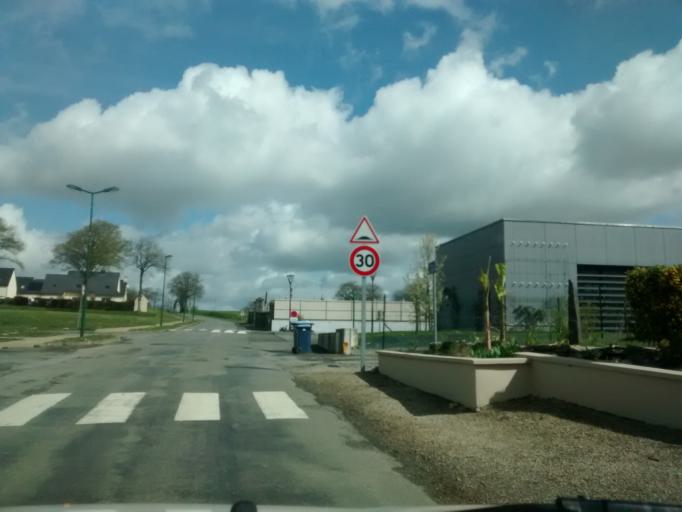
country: FR
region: Brittany
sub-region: Departement d'Ille-et-Vilaine
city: Livre-sur-Changeon
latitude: 48.1938
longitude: -1.3687
